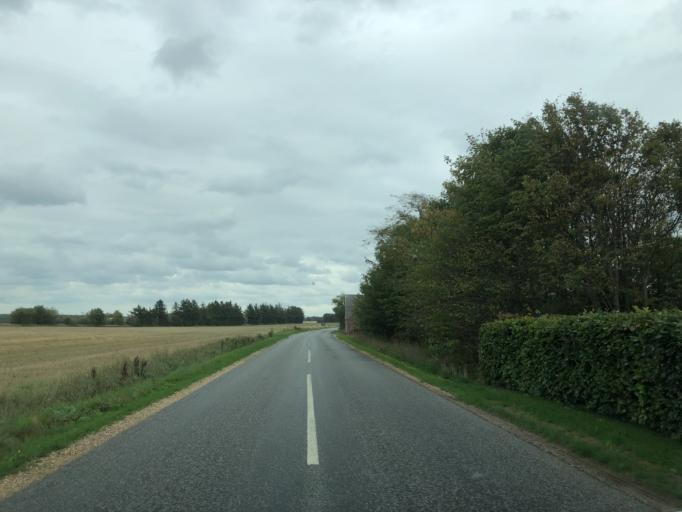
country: DK
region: Central Jutland
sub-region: Herning Kommune
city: Lind
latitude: 56.0898
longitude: 8.9356
